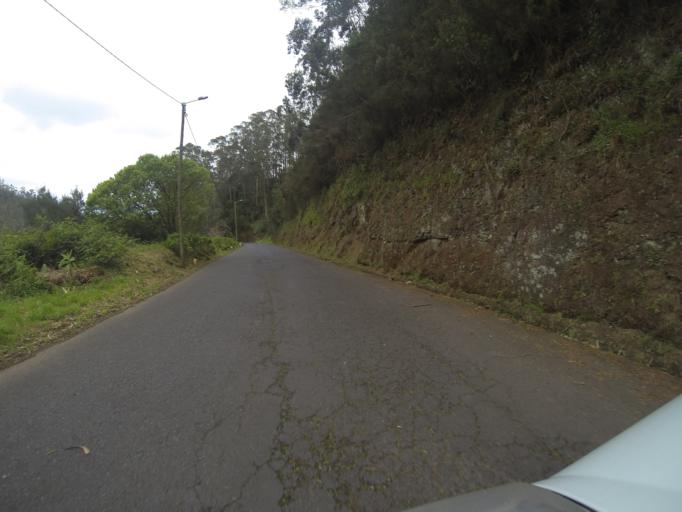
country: PT
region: Madeira
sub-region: Santa Cruz
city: Santa Cruz
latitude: 32.7413
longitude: -16.8245
